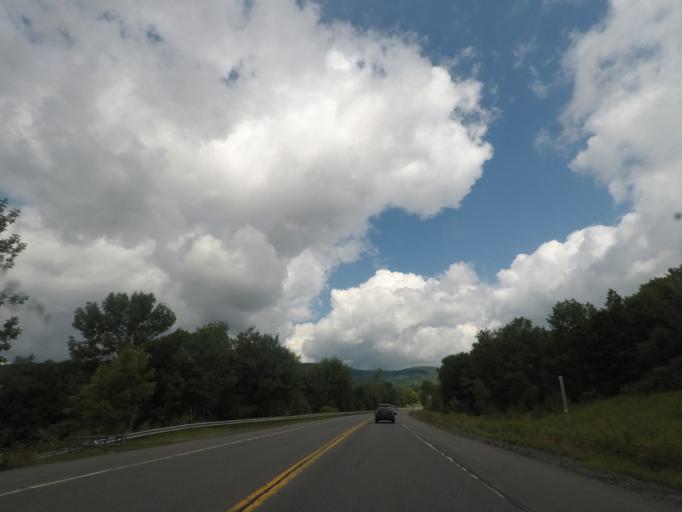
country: US
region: Massachusetts
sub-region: Berkshire County
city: Lanesborough
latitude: 42.6084
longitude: -73.3754
